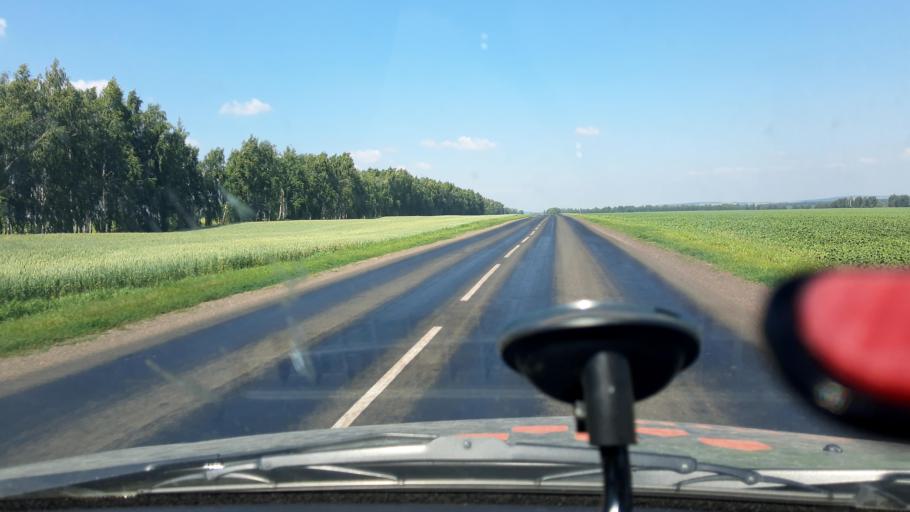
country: RU
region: Bashkortostan
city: Chekmagush
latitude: 55.0871
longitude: 54.6406
